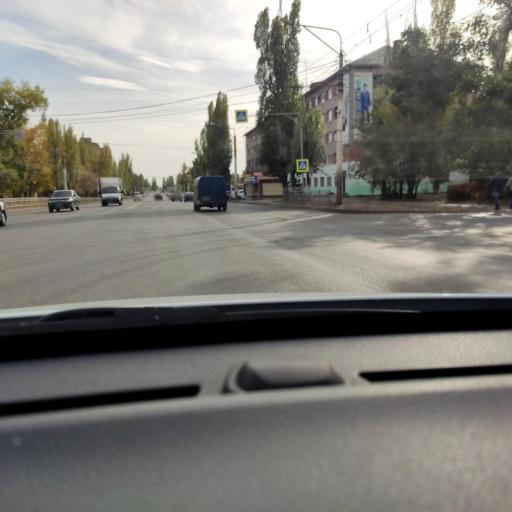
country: RU
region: Voronezj
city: Maslovka
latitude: 51.6101
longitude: 39.2372
